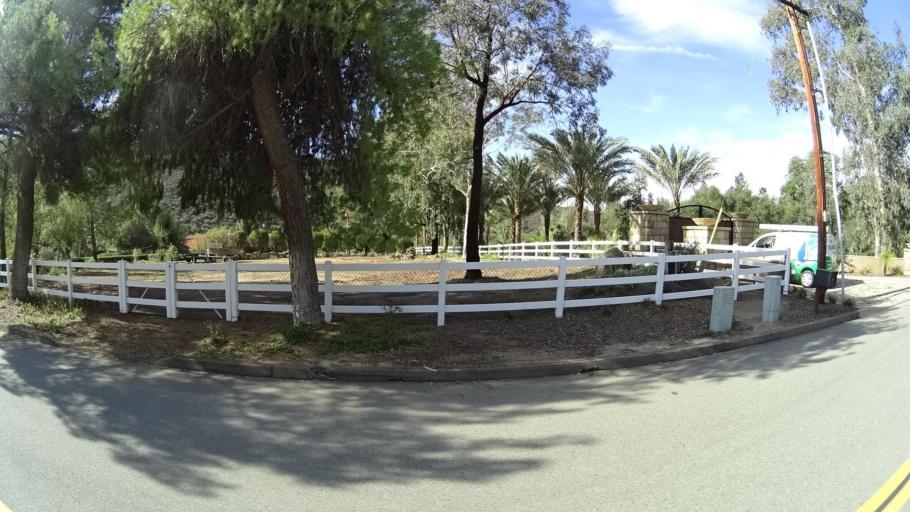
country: US
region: California
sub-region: San Diego County
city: Alpine
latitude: 32.8140
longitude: -116.7209
